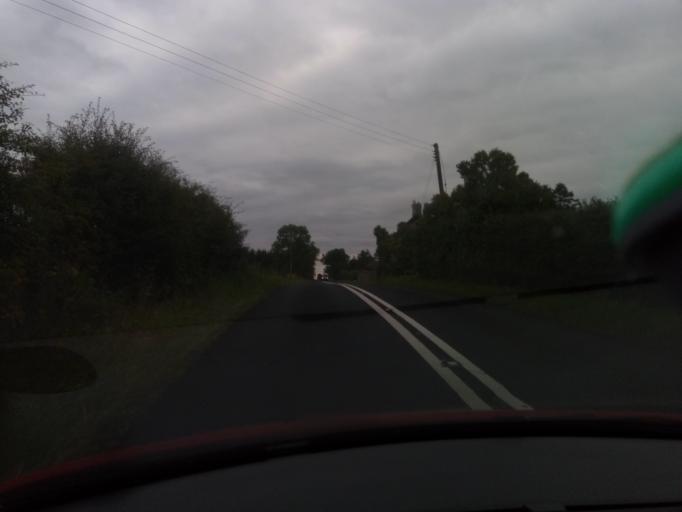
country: GB
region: England
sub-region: Northumberland
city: Warden
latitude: 54.9578
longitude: -2.1689
